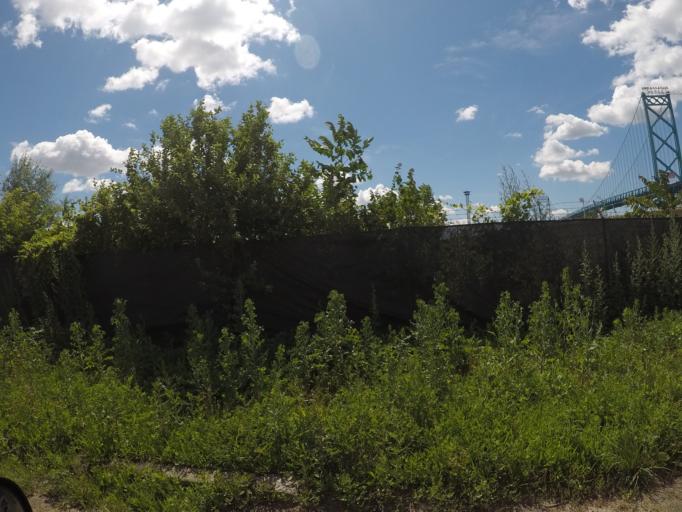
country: US
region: Michigan
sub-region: Wayne County
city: Detroit
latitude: 42.3173
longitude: -83.0756
